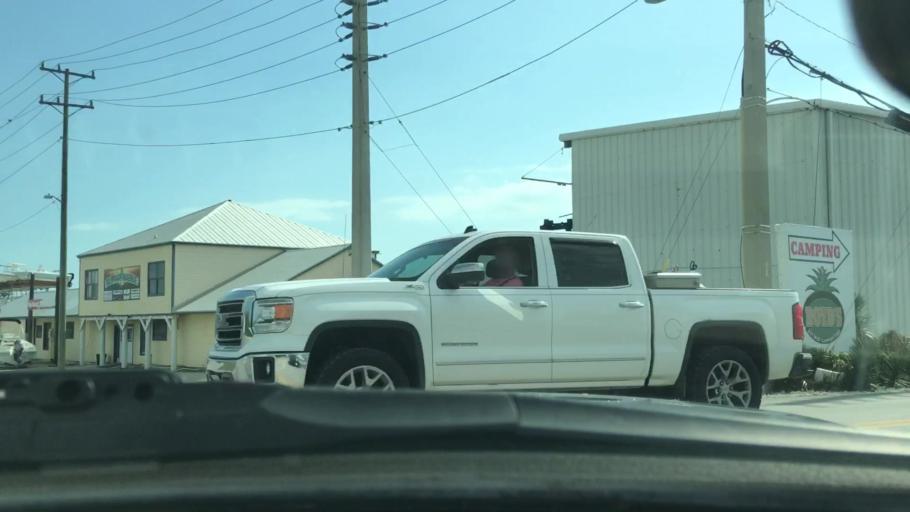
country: US
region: Florida
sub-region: Monroe County
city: Stock Island
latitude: 24.5745
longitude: -81.7360
